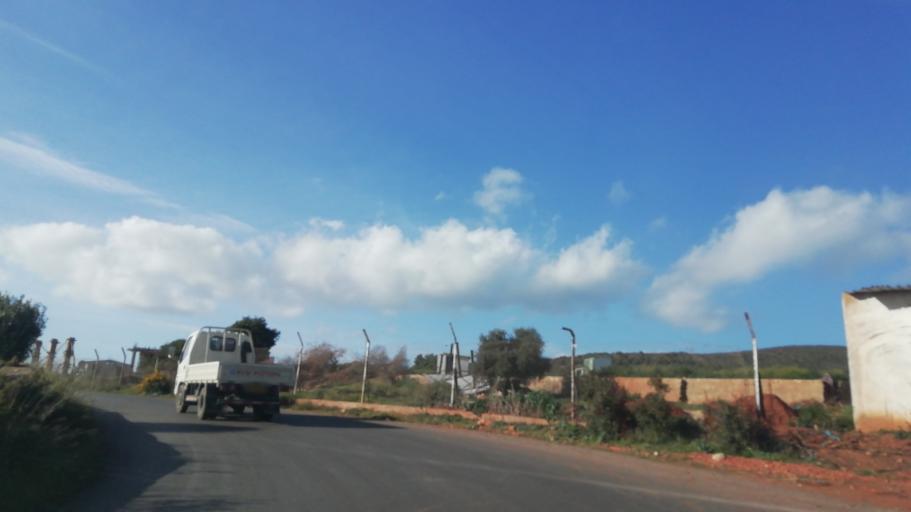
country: DZ
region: Oran
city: Bir el Djir
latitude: 35.7520
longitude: -0.5116
